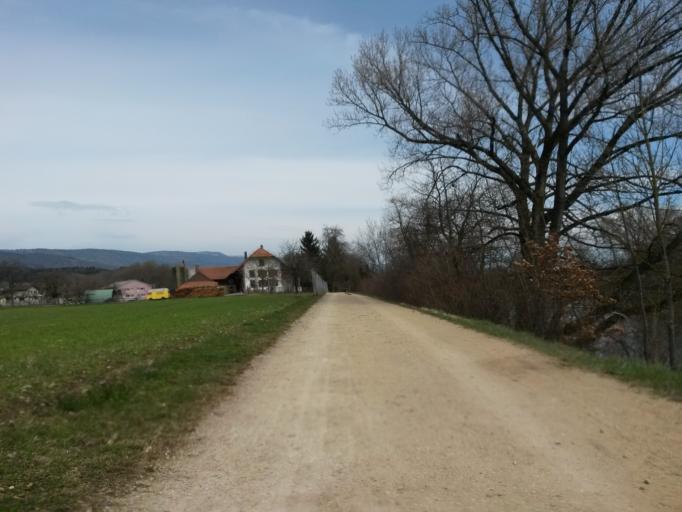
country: CH
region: Bern
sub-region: Biel/Bienne District
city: Orpund
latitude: 47.1308
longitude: 7.3018
